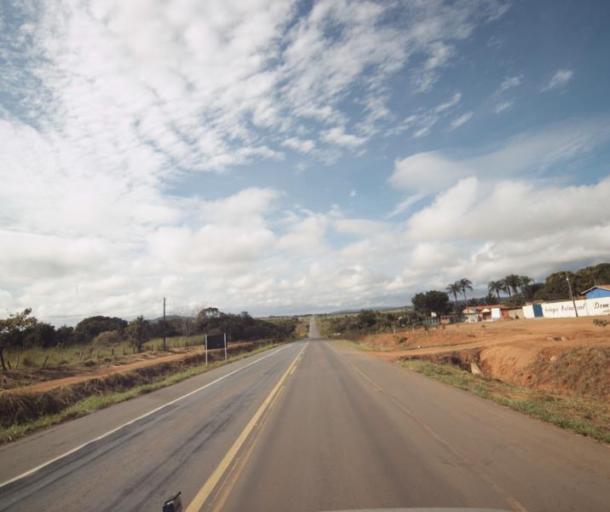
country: BR
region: Goias
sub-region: Barro Alto
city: Barro Alto
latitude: -15.2108
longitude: -48.6993
